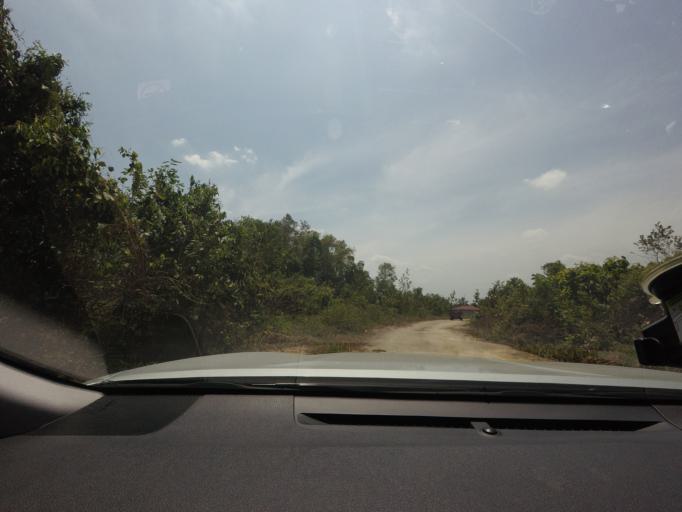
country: TH
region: Narathiwat
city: Rueso
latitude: 6.3848
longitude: 101.5101
